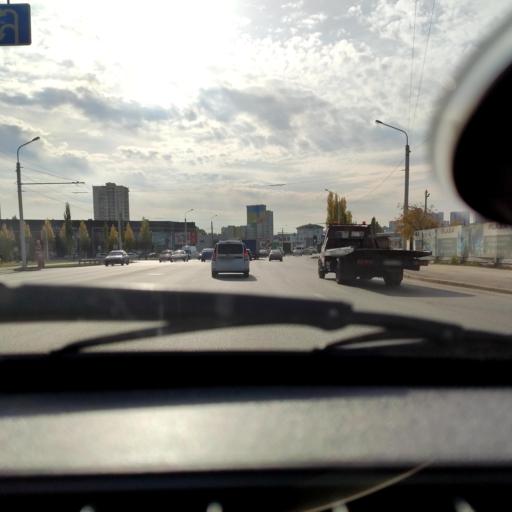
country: RU
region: Bashkortostan
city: Ufa
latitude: 54.7755
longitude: 56.0668
